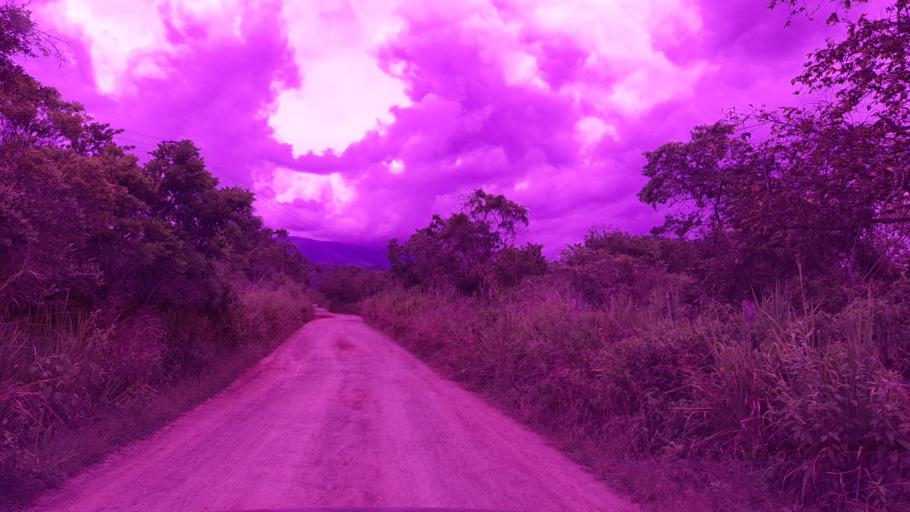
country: CO
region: Valle del Cauca
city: Bugalagrande
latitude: 4.1893
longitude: -76.1398
